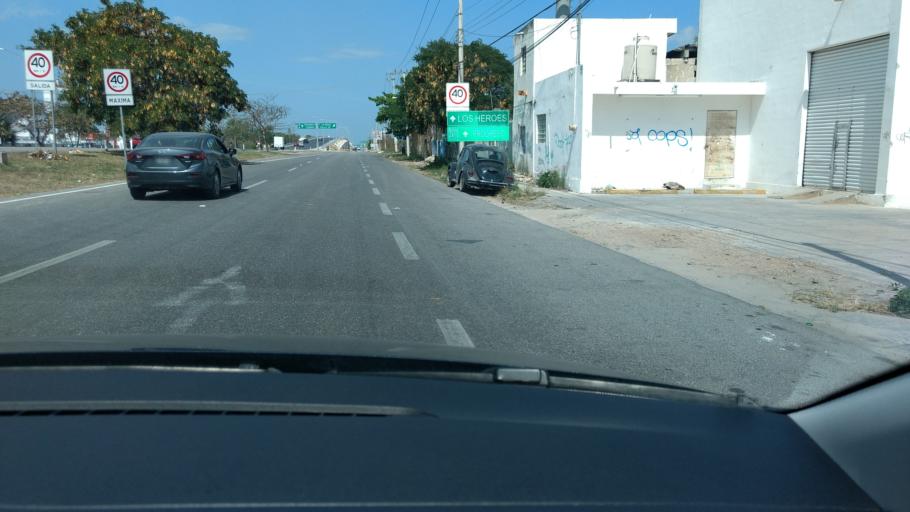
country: MX
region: Yucatan
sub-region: Kanasin
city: Kanasin
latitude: 20.9761
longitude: -89.5643
